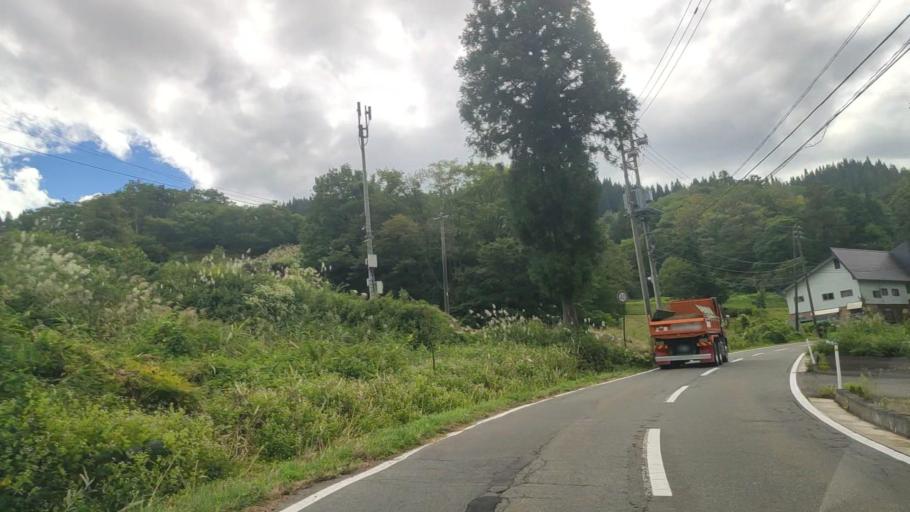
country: JP
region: Nagano
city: Iiyama
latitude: 36.8813
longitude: 138.3208
